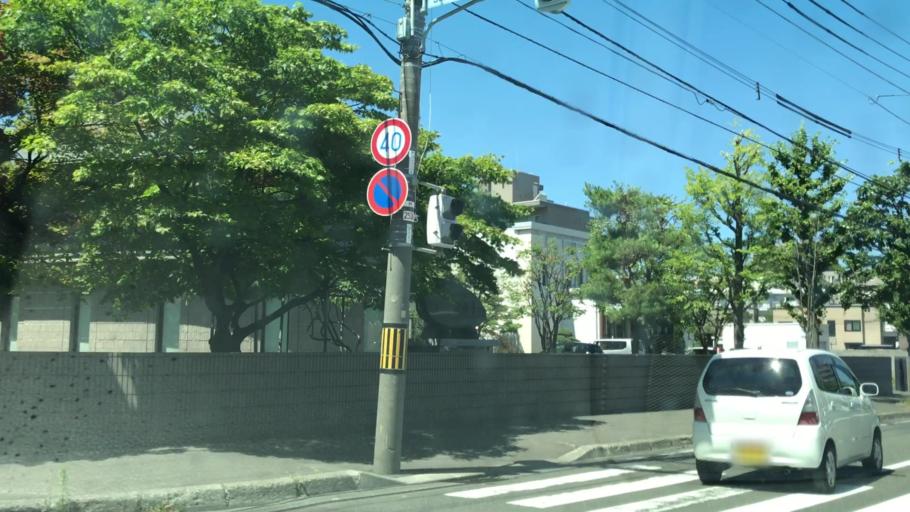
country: JP
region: Hokkaido
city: Sapporo
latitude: 43.0500
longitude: 141.3218
